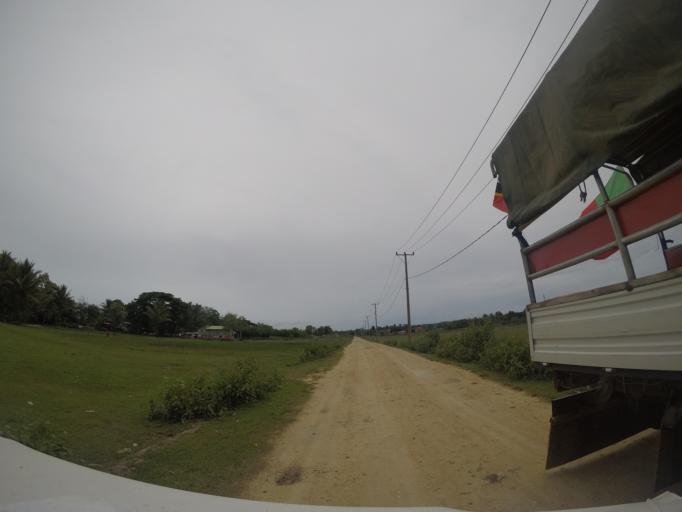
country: TL
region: Lautem
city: Lospalos
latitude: -8.5225
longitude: 127.0033
